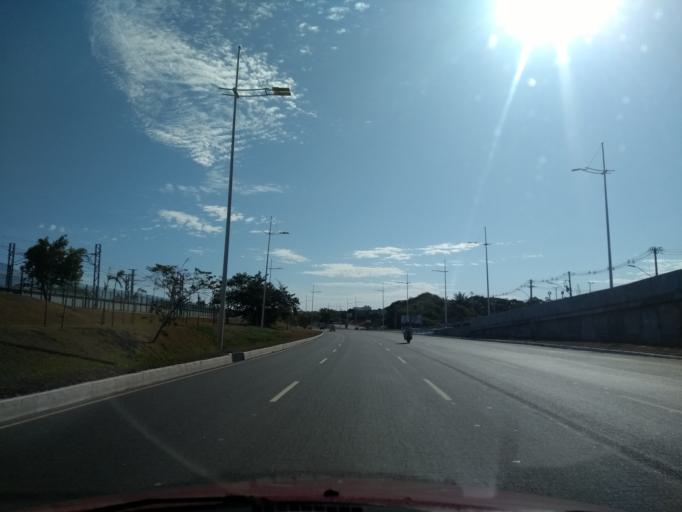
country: BR
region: Bahia
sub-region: Lauro De Freitas
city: Lauro de Freitas
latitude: -12.9264
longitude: -38.3846
